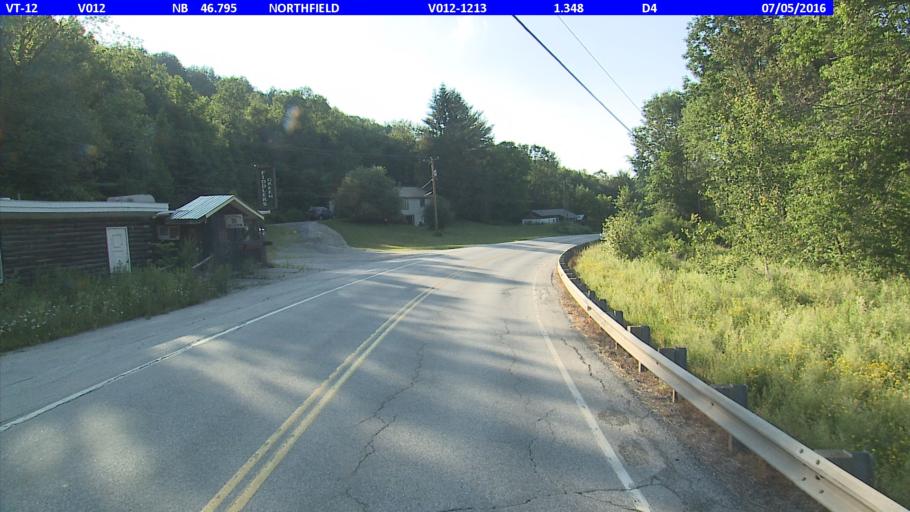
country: US
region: Vermont
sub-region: Washington County
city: Northfield
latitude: 44.1099
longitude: -72.6497
